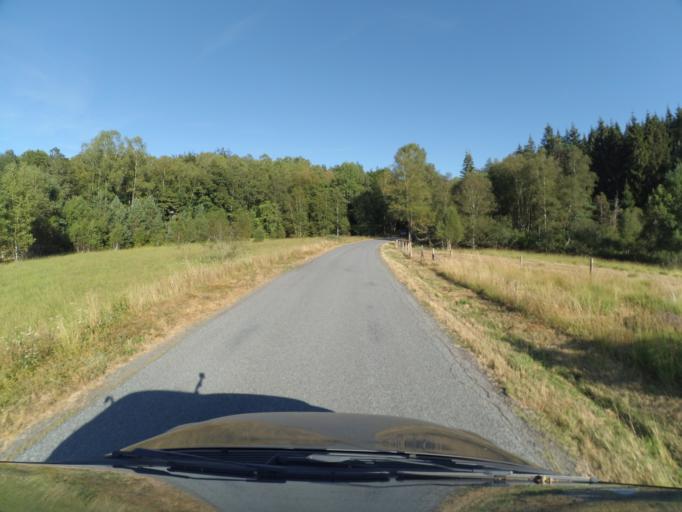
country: FR
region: Limousin
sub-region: Departement de la Creuse
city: Banize
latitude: 45.7902
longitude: 1.9680
